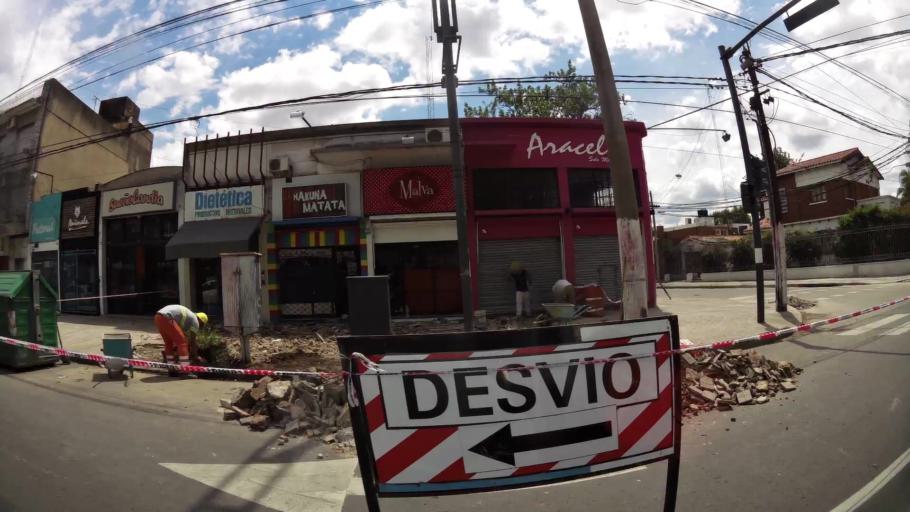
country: AR
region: Santa Fe
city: Gobernador Galvez
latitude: -32.9951
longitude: -60.6477
